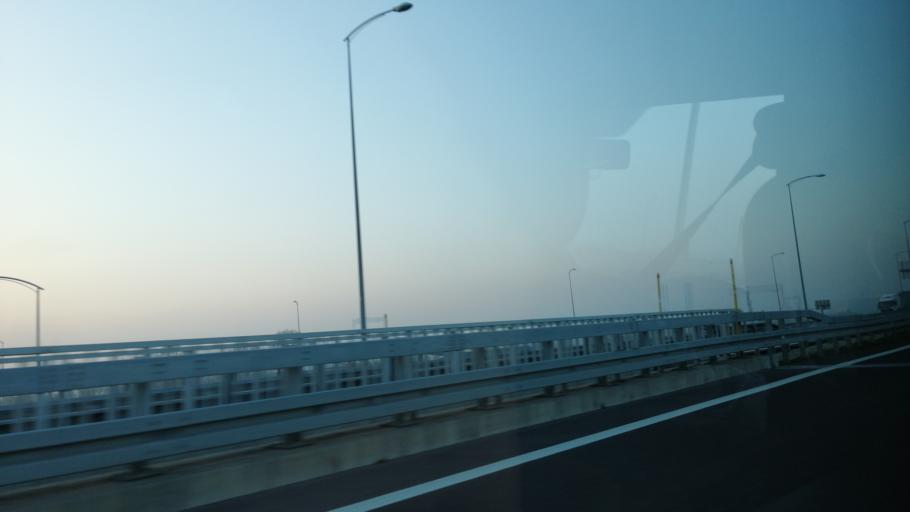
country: TR
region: Yalova
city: Altinova
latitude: 40.6908
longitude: 29.4707
